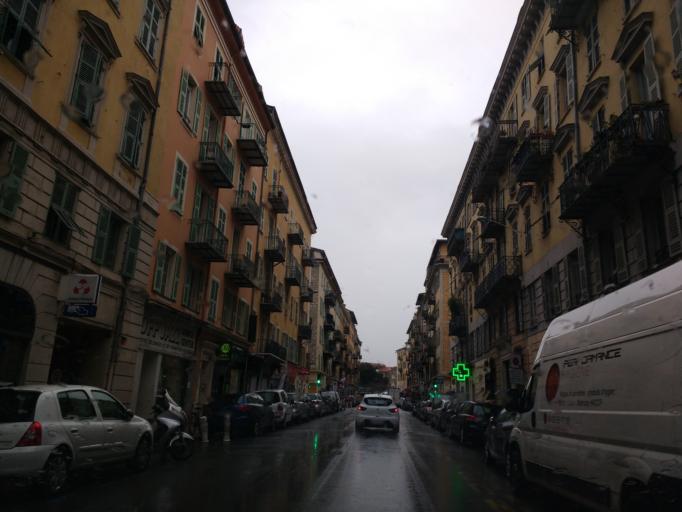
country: FR
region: Provence-Alpes-Cote d'Azur
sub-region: Departement des Alpes-Maritimes
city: Nice
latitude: 43.6997
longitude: 7.2827
